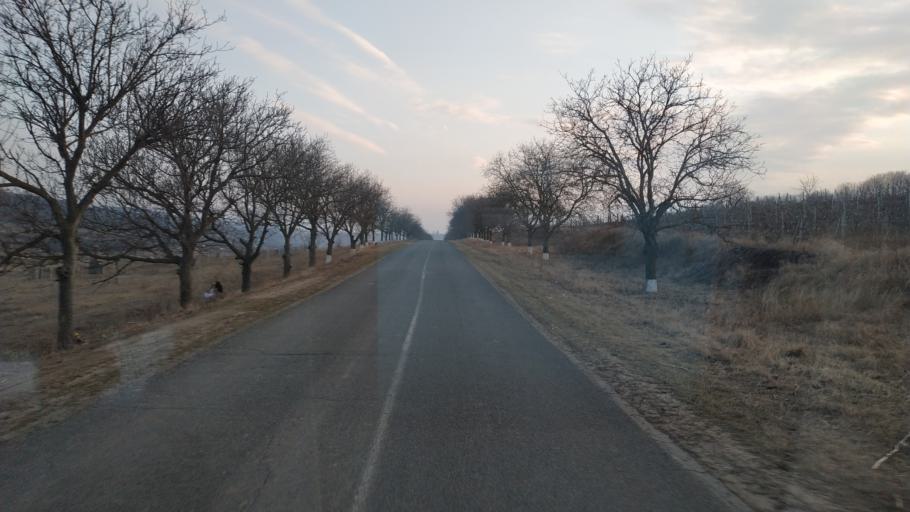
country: MD
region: Hincesti
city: Dancu
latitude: 46.6867
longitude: 28.3358
